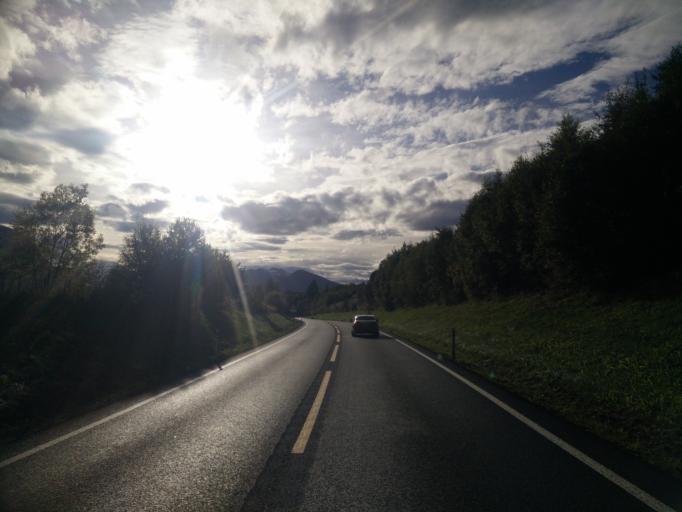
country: NO
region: More og Romsdal
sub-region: Vestnes
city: Vestnes
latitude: 62.6147
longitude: 7.0885
